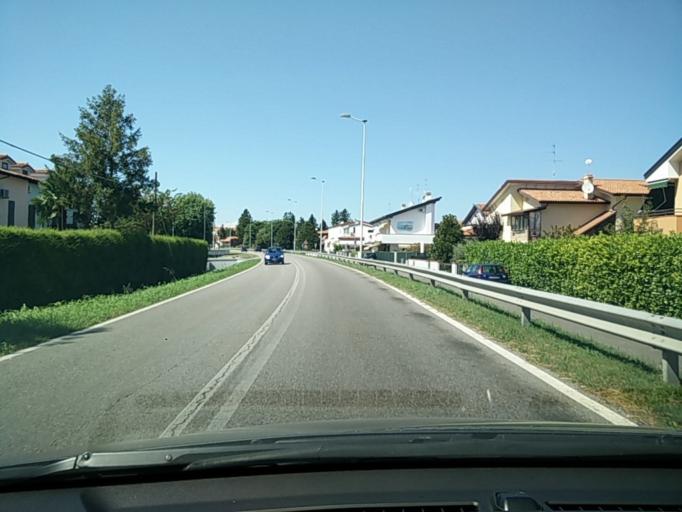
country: IT
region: Veneto
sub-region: Provincia di Venezia
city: La Salute di Livenza
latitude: 45.6457
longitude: 12.8430
